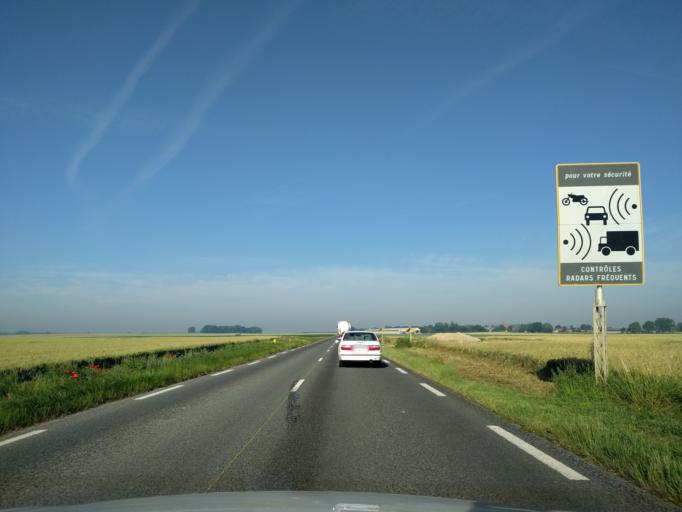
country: FR
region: Picardie
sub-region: Departement de la Somme
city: Roye
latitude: 49.6614
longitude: 2.7224
